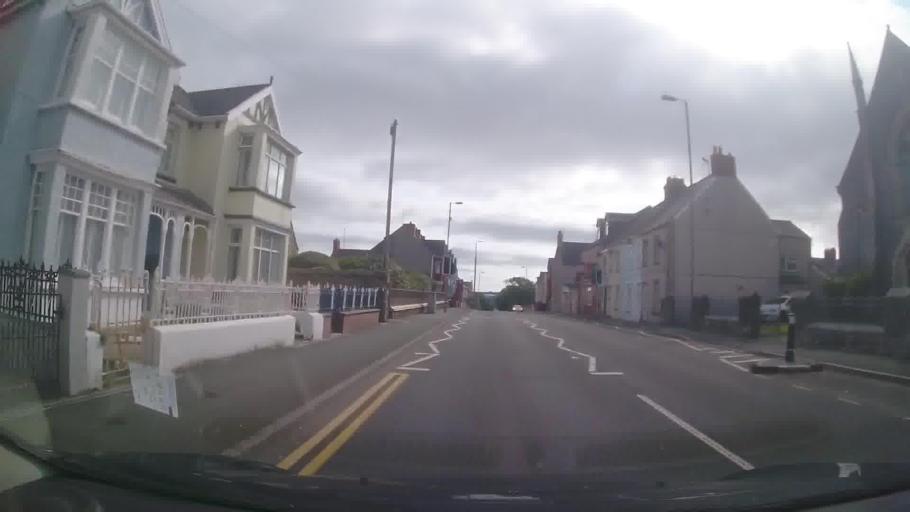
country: GB
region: Wales
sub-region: Pembrokeshire
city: Milford Haven
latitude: 51.7140
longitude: -5.0284
